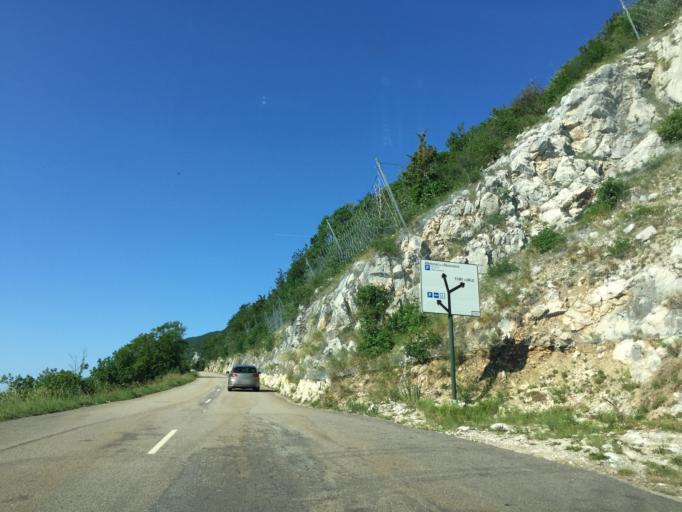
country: FR
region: Rhone-Alpes
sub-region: Departement de la Drome
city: Saint-Laurent-en-Royans
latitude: 44.9111
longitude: 5.3648
